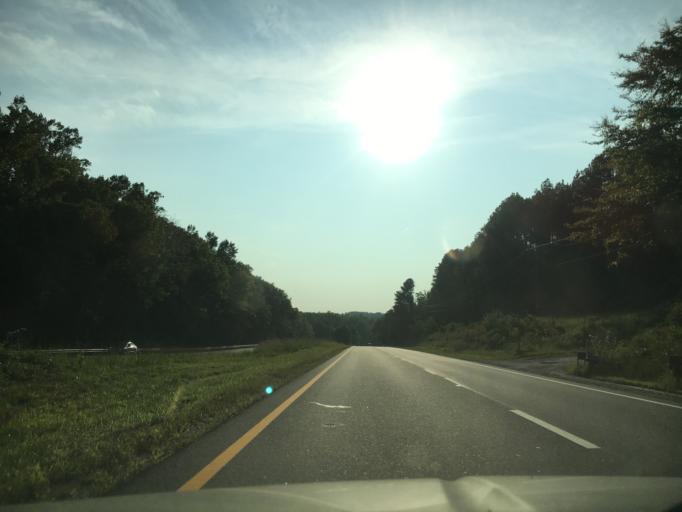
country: US
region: Virginia
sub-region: Prince Edward County
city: Farmville
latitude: 37.2783
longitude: -78.3421
